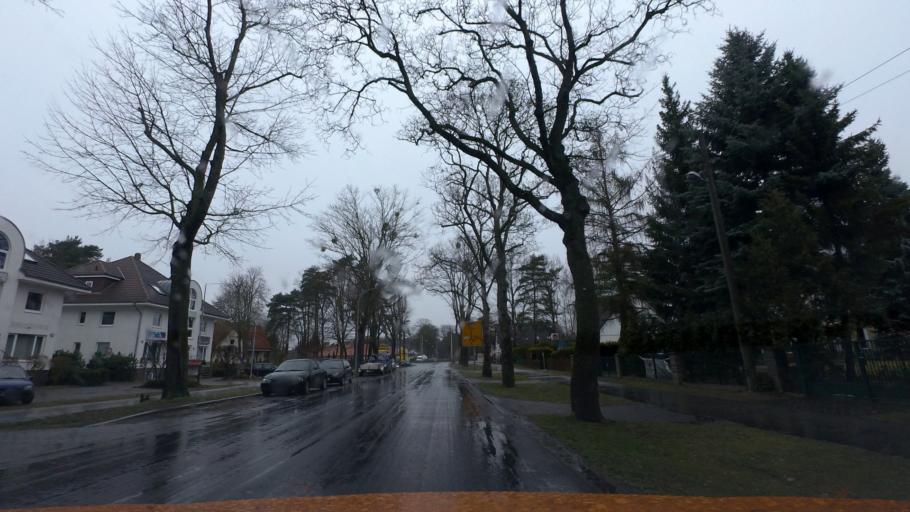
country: DE
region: Brandenburg
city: Falkensee
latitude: 52.5799
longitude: 13.0758
